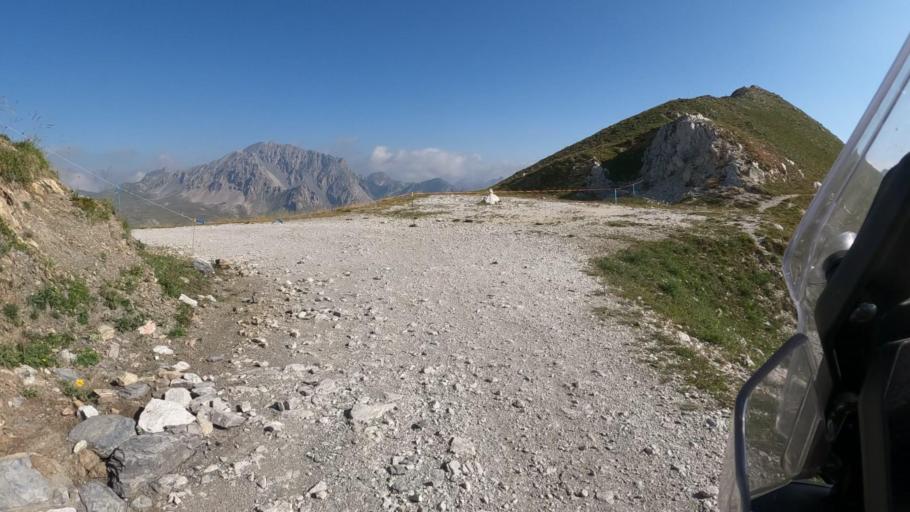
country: IT
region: Piedmont
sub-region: Provincia di Cuneo
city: Pietraporzio
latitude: 44.3881
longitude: 7.0430
